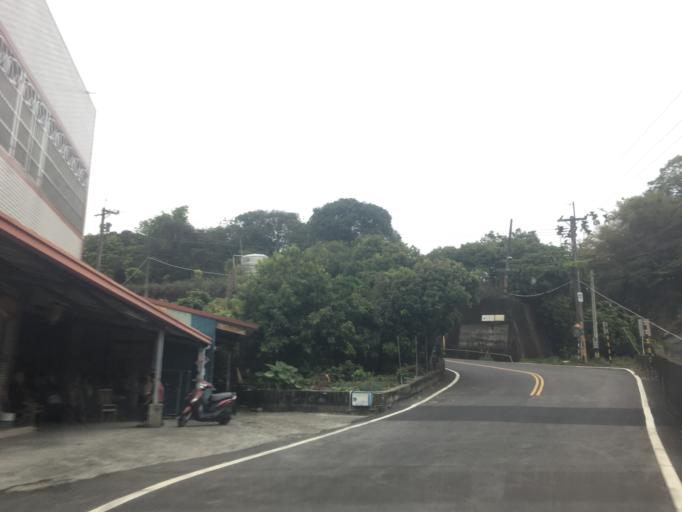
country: TW
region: Taiwan
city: Zhongxing New Village
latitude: 24.0355
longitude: 120.7364
